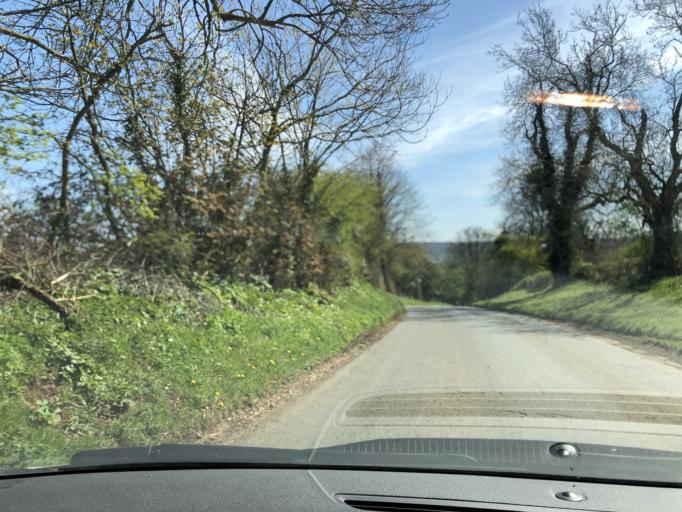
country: GB
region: England
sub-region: Oxfordshire
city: Hook Norton
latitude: 52.0087
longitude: -1.4406
